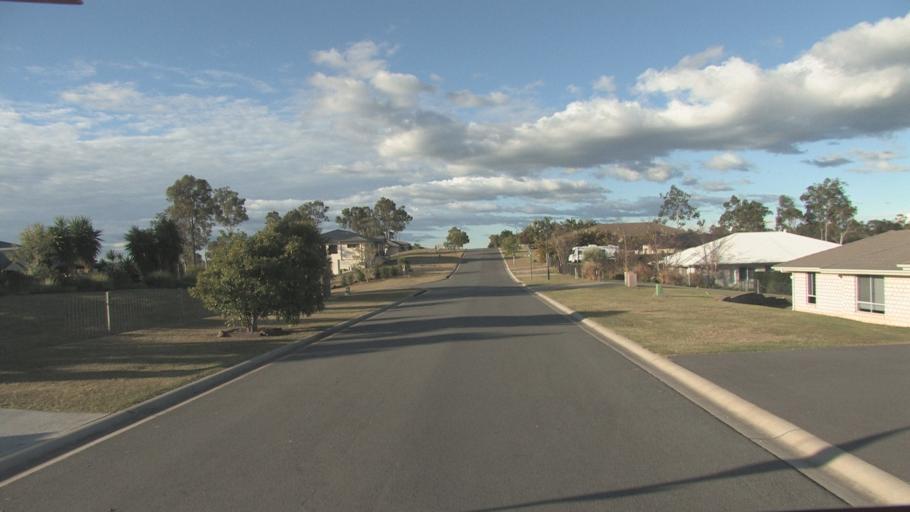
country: AU
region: Queensland
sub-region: Logan
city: Cedar Vale
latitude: -27.8667
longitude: 153.0817
